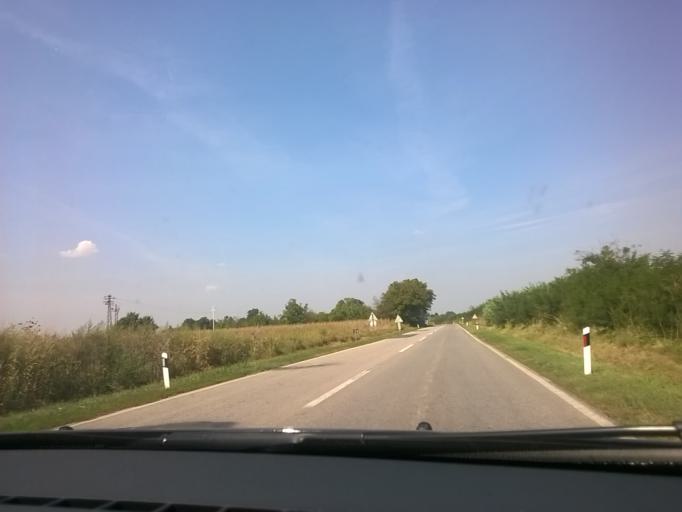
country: RS
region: Autonomna Pokrajina Vojvodina
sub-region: Juznobanatski Okrug
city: Vrsac
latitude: 45.1223
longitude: 21.2765
